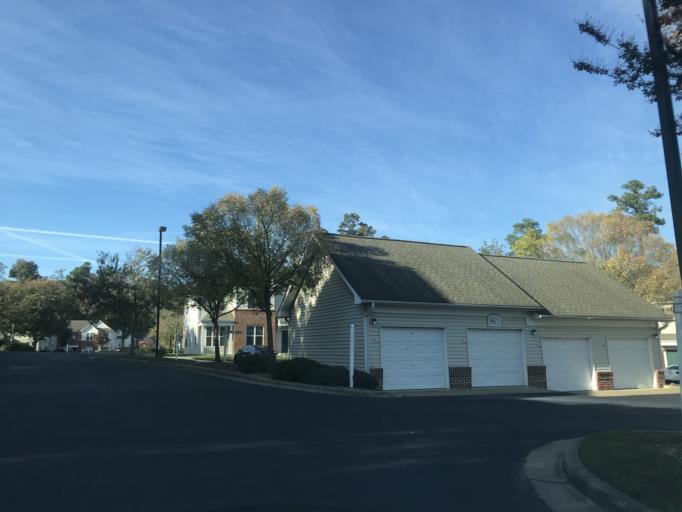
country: US
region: North Carolina
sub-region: Wake County
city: Wake Forest
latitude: 35.8999
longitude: -78.5525
